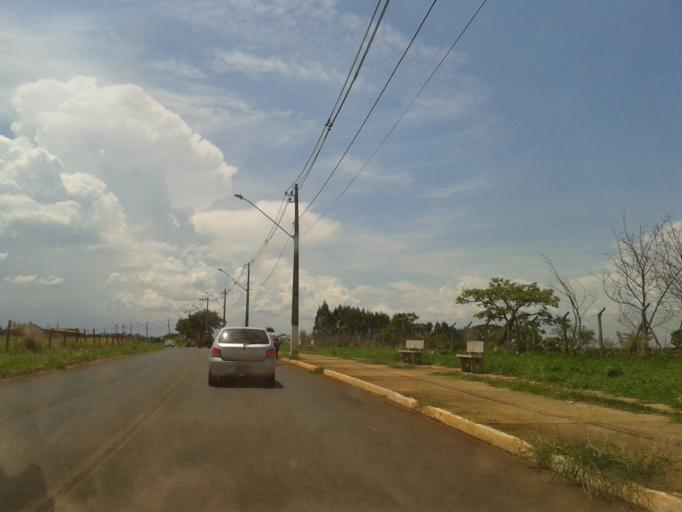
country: BR
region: Minas Gerais
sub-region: Araguari
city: Araguari
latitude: -18.6753
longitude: -48.1953
